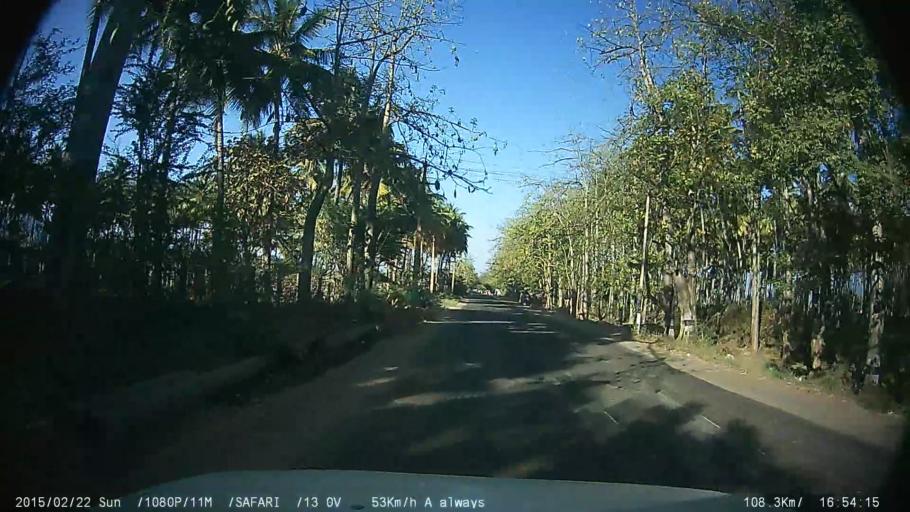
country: IN
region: Tamil Nadu
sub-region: Theni
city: Gudalur
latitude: 9.6700
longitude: 77.2357
